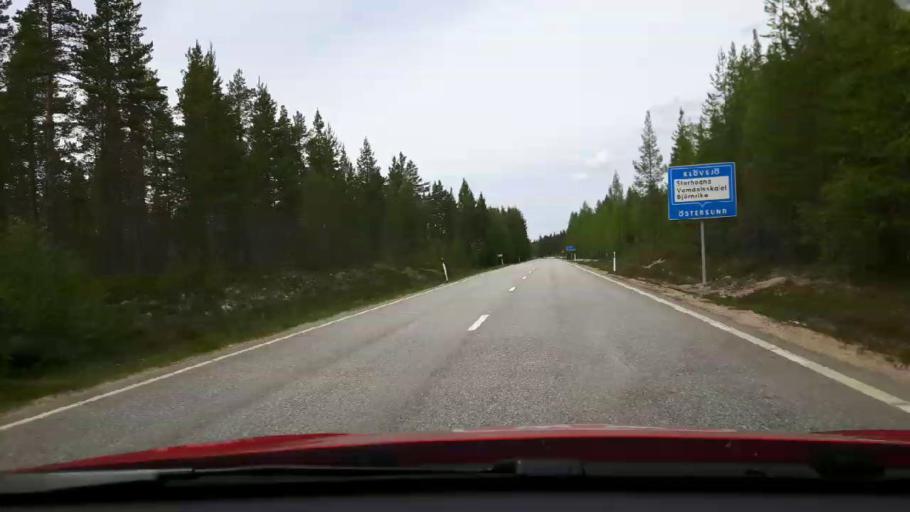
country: SE
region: Jaemtland
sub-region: Harjedalens Kommun
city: Sveg
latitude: 62.1171
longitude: 14.1737
